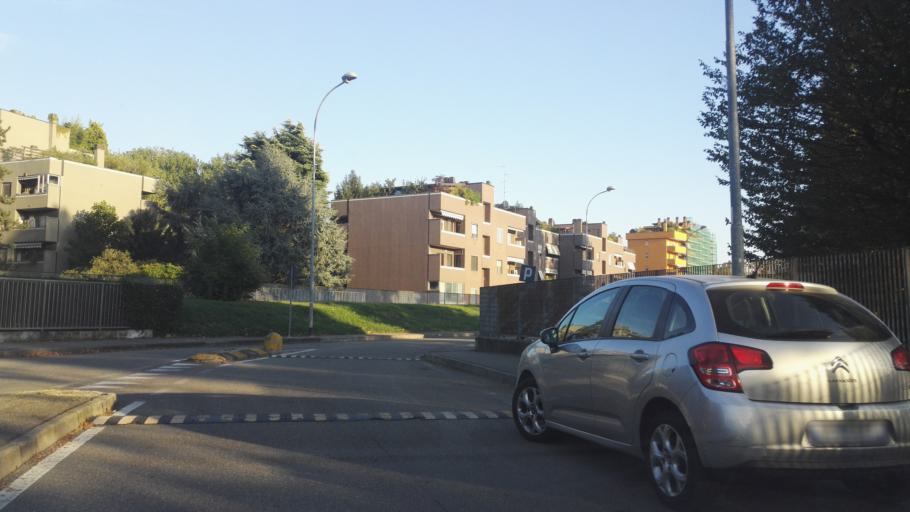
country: IT
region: Lombardy
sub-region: Citta metropolitana di Milano
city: San Bovio-San Felice
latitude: 45.4603
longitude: 9.3159
